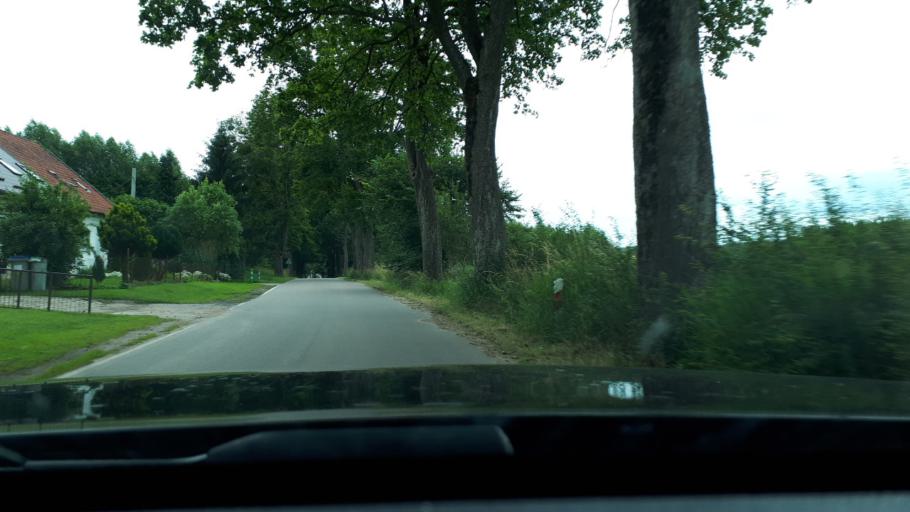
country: PL
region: Warmian-Masurian Voivodeship
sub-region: Powiat ostrodzki
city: Ostroda
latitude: 53.6852
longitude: 20.0587
